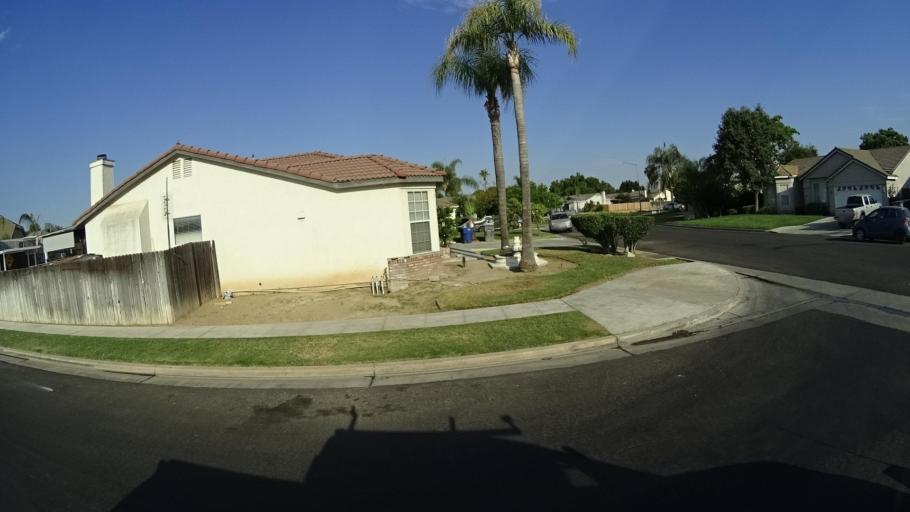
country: US
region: California
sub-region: Fresno County
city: Sunnyside
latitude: 36.7114
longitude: -119.6956
